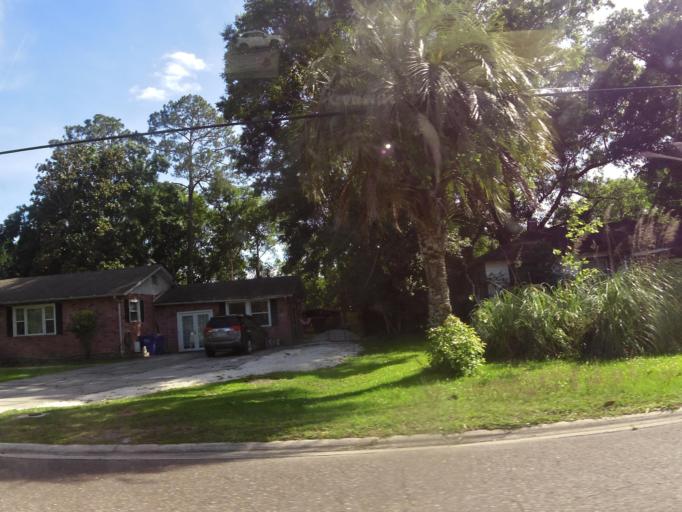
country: US
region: Florida
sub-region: Nassau County
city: Callahan
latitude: 30.5580
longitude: -81.8283
